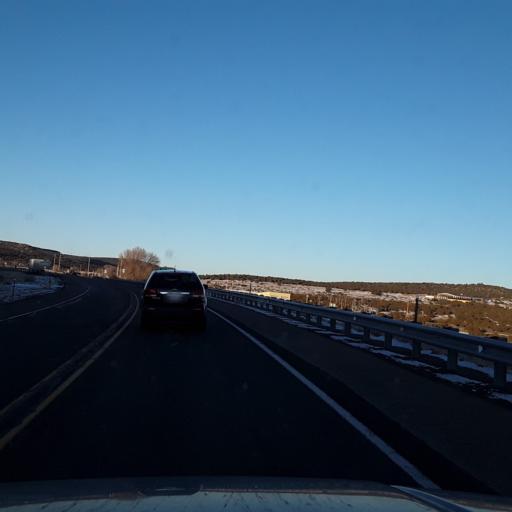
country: US
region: New Mexico
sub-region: Lincoln County
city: Carrizozo
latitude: 34.2422
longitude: -105.5963
